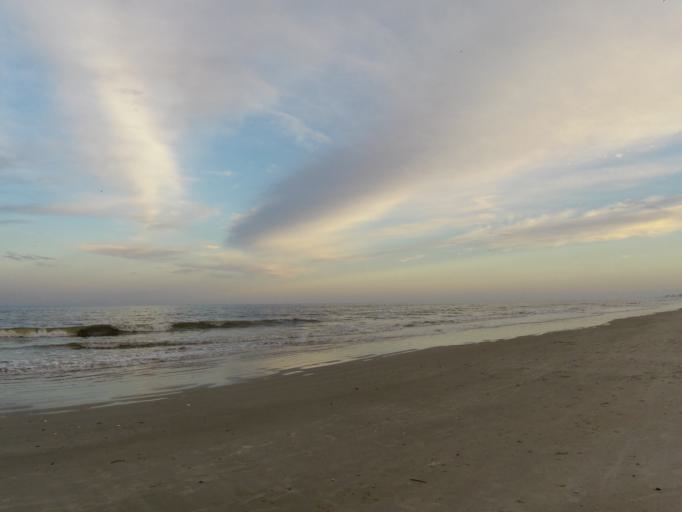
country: US
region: Florida
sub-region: Duval County
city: Atlantic Beach
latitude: 30.3616
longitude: -81.3972
